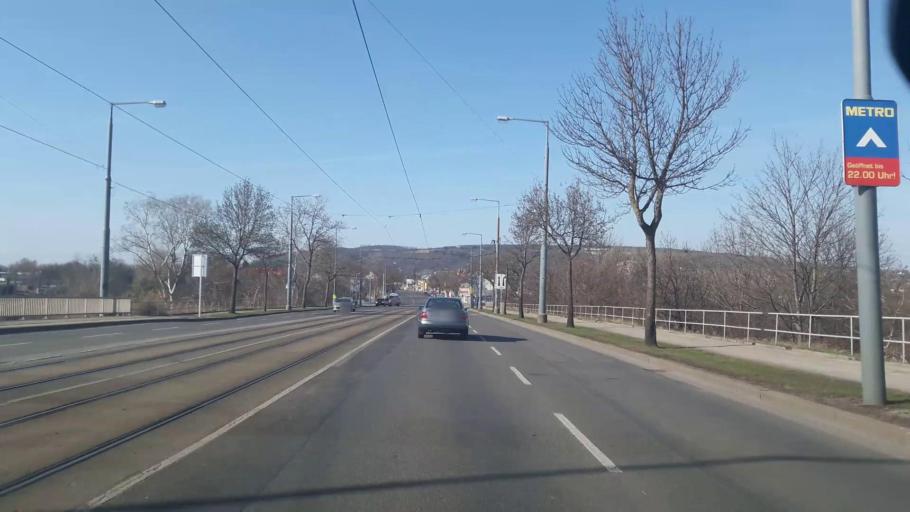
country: AT
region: Lower Austria
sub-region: Politischer Bezirk Korneuburg
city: Langenzersdorf
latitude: 48.2826
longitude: 16.3858
